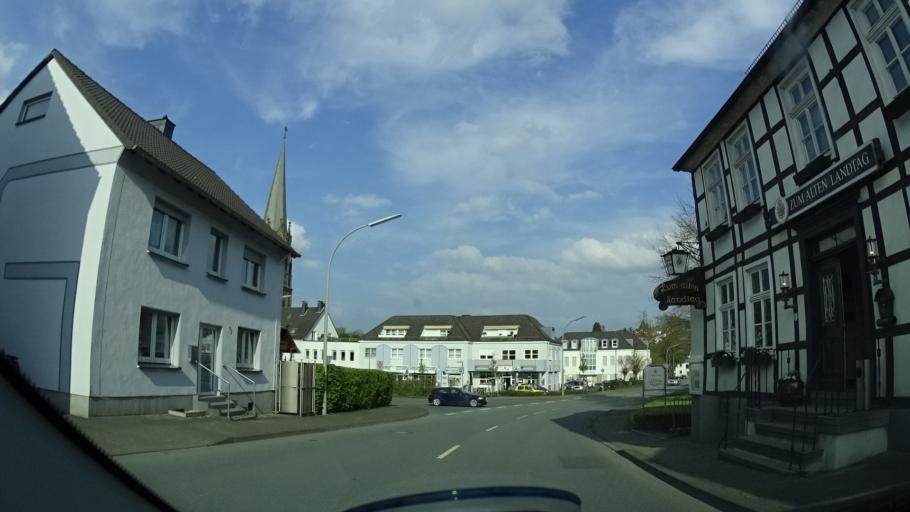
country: DE
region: North Rhine-Westphalia
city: Warstein
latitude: 51.4422
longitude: 8.3505
